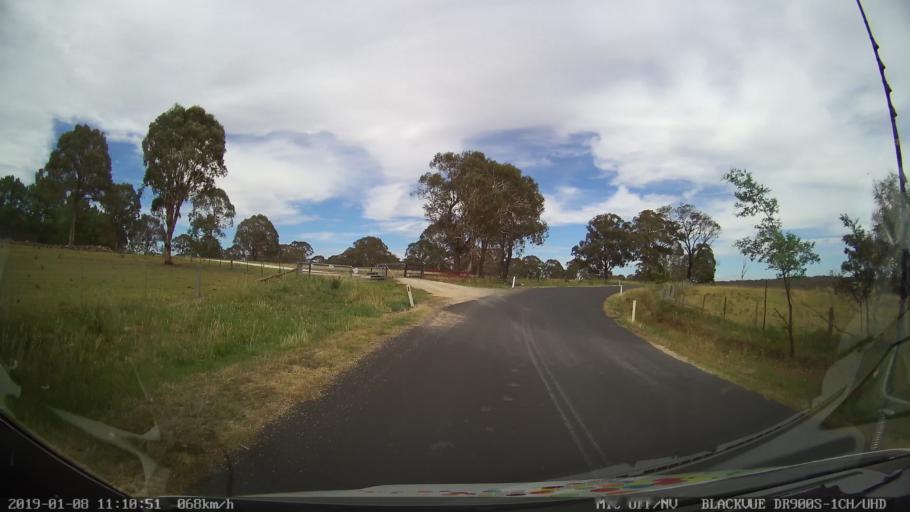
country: AU
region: New South Wales
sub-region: Guyra
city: Guyra
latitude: -30.2265
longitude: 151.6316
